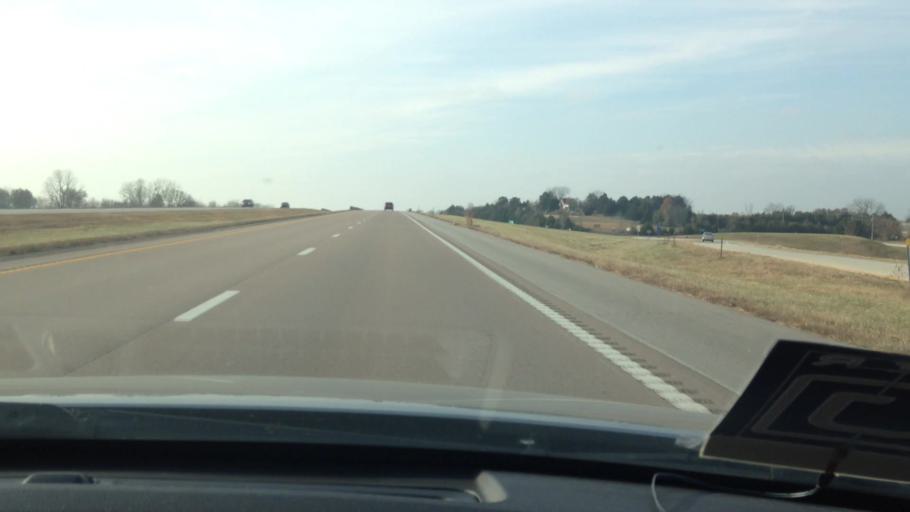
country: US
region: Missouri
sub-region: Cass County
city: Garden City
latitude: 38.4658
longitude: -93.9993
